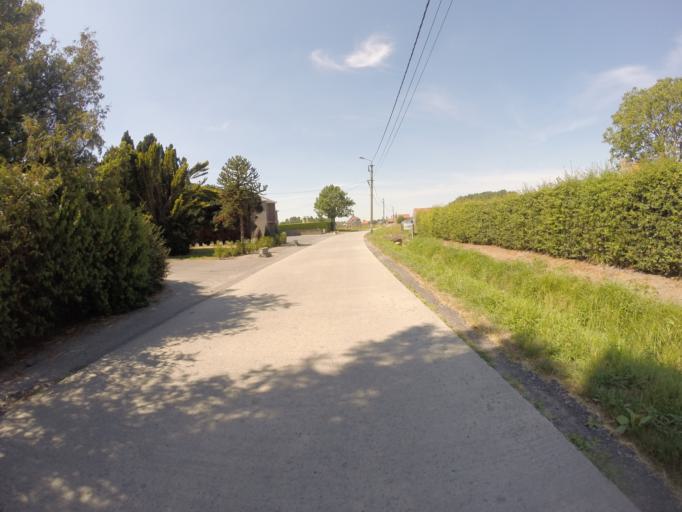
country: BE
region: Flanders
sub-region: Provincie Oost-Vlaanderen
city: Knesselare
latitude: 51.1281
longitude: 3.4029
